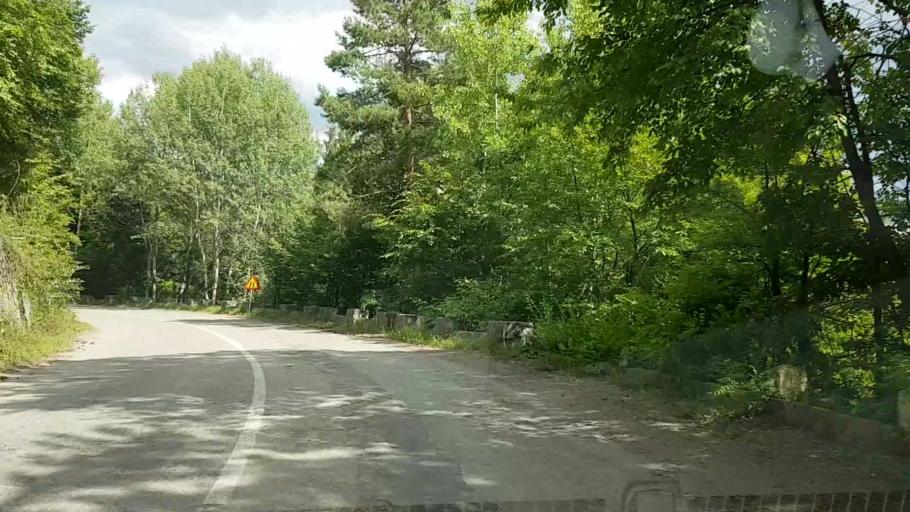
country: RO
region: Neamt
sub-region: Comuna Ceahlau
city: Ceahlau
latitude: 47.0536
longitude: 25.9950
